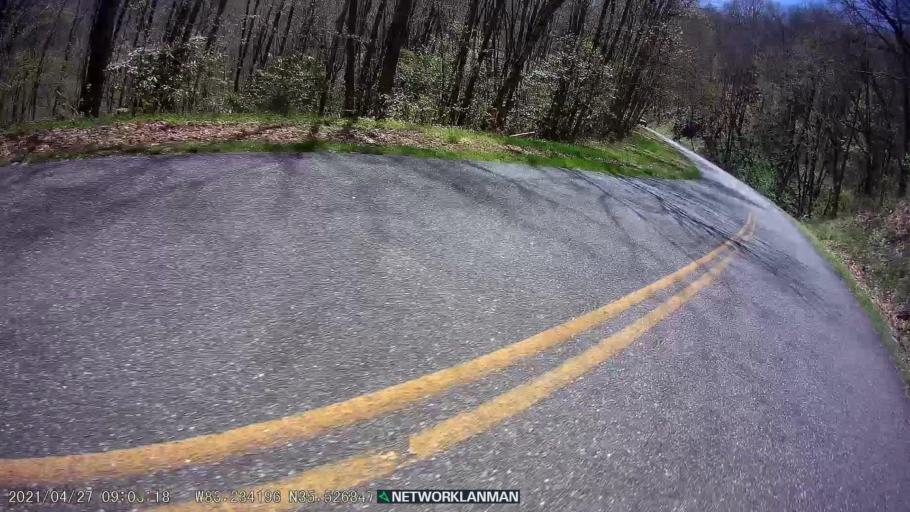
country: US
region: North Carolina
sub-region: Swain County
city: Cherokee
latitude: 35.5268
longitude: -83.2342
